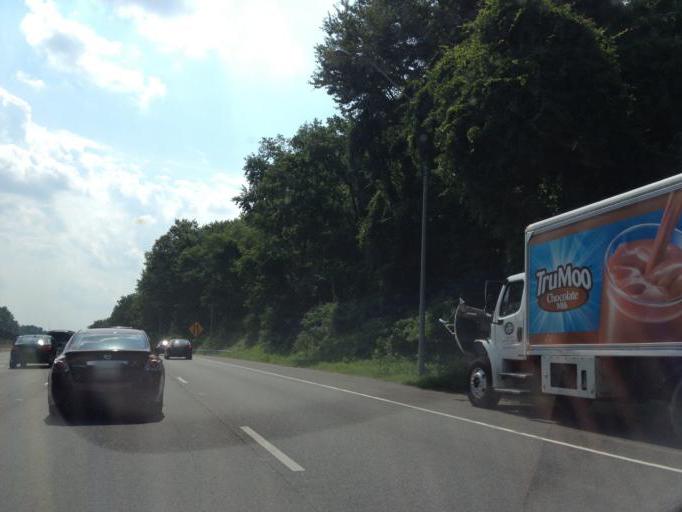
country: US
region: Maryland
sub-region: Montgomery County
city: Hillandale
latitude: 39.0197
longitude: -76.9864
